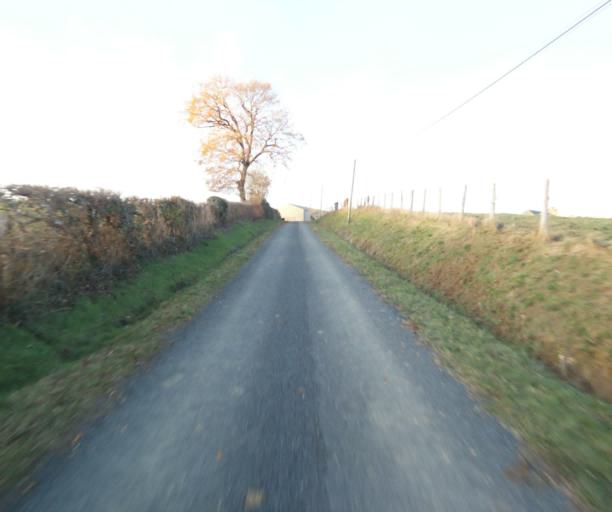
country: FR
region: Limousin
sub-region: Departement de la Correze
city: Laguenne
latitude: 45.2364
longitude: 1.8264
